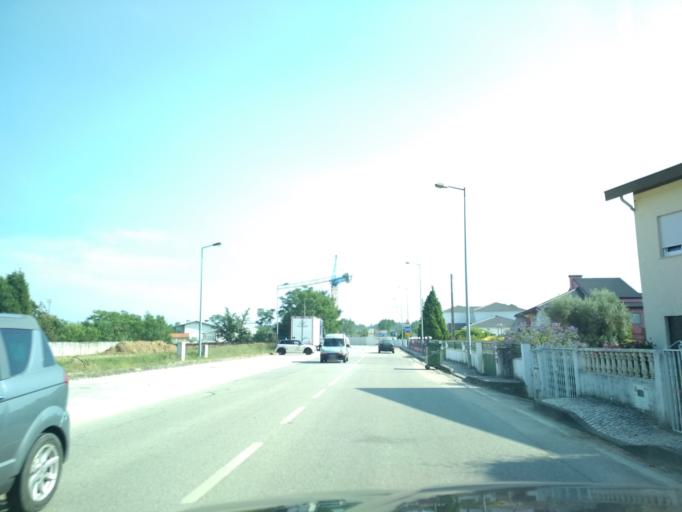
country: PT
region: Aveiro
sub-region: Mealhada
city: Mealhada
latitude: 40.3777
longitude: -8.4577
